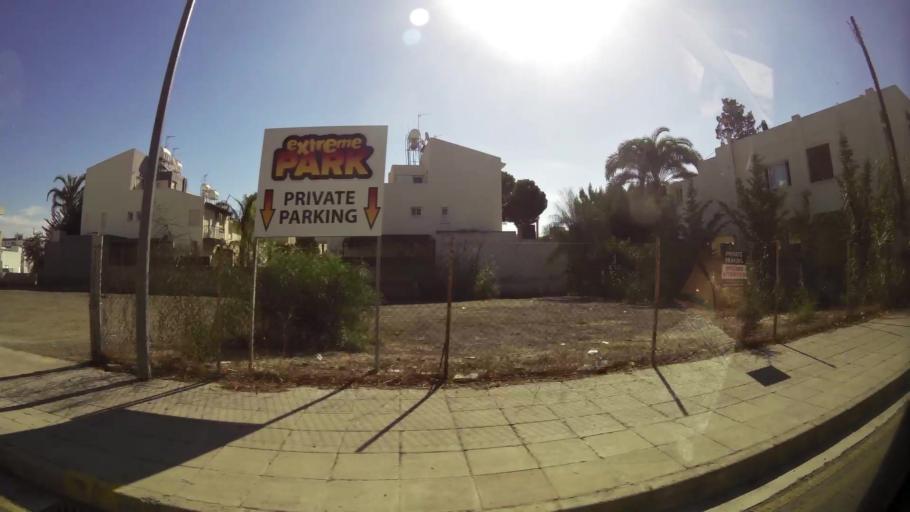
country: CY
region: Lefkosia
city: Nicosia
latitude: 35.1396
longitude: 33.3369
